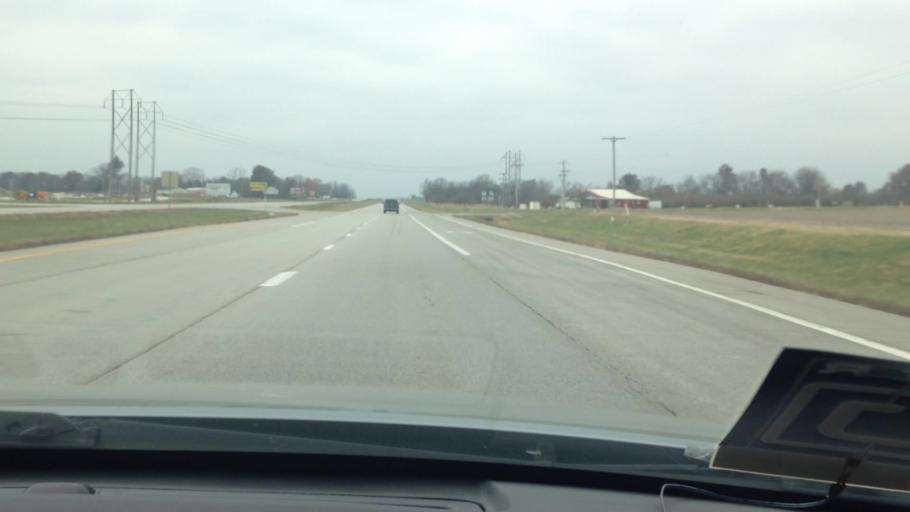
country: US
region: Missouri
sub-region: Cass County
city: Garden City
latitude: 38.5942
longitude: -94.2462
